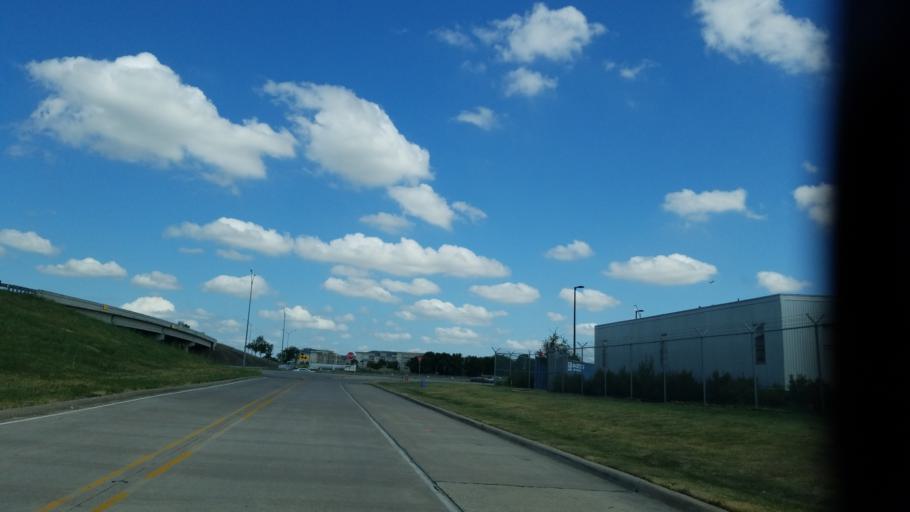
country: US
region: Texas
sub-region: Tarrant County
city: Euless
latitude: 32.8358
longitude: -97.0689
